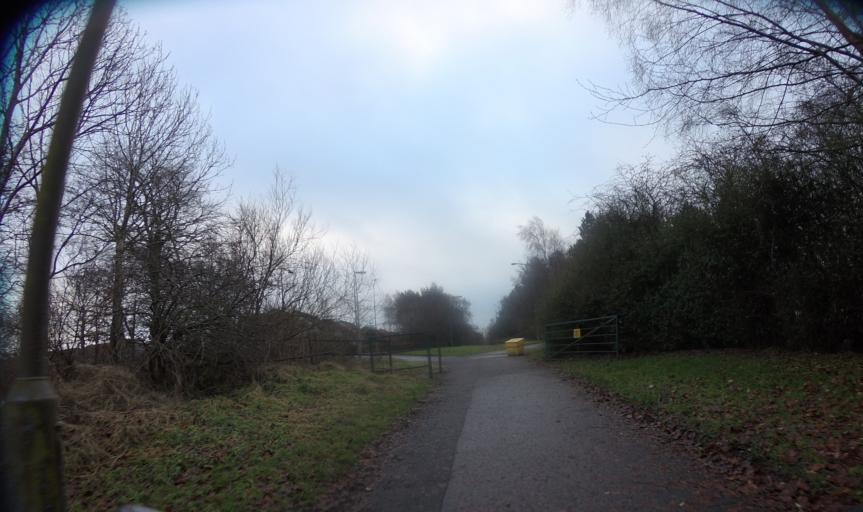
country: GB
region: Scotland
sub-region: West Lothian
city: Livingston
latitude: 55.8738
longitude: -3.5336
